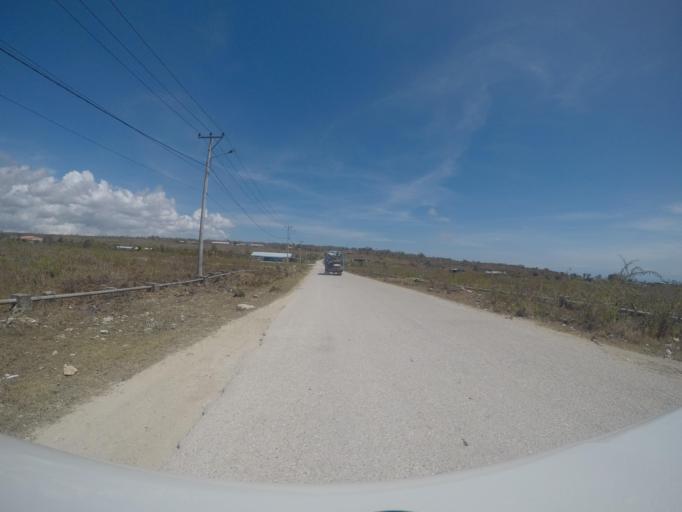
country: TL
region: Baucau
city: Baucau
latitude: -8.4728
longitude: 126.4426
